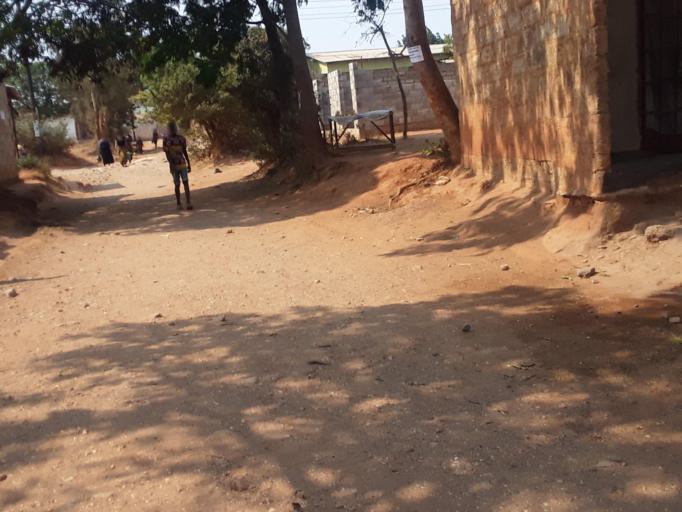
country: ZM
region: Lusaka
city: Lusaka
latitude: -15.3547
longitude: 28.2969
